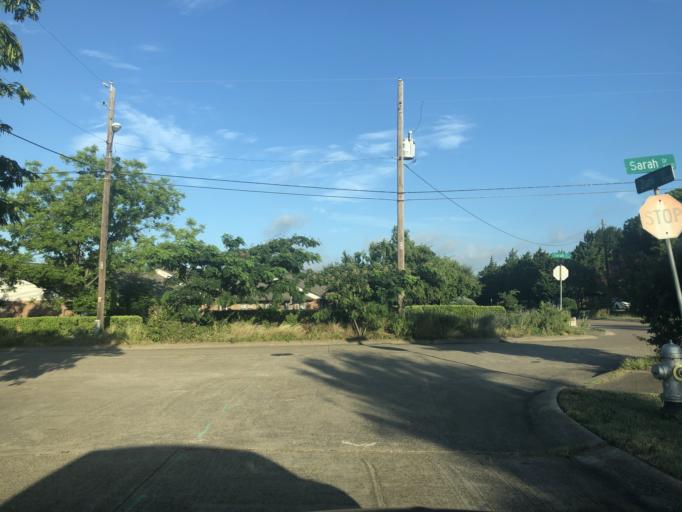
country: US
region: Texas
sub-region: Dallas County
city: Duncanville
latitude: 32.6667
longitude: -96.9519
